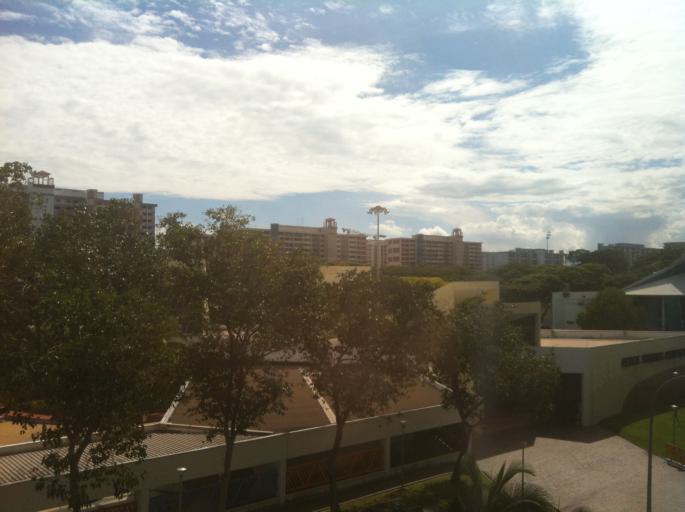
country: SG
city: Singapore
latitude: 1.3249
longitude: 103.9364
